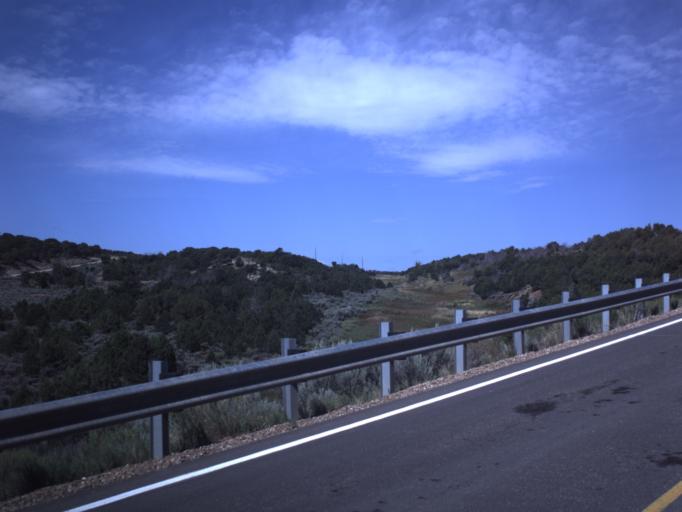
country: US
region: Utah
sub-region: Duchesne County
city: Duchesne
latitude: 40.3251
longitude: -110.4053
